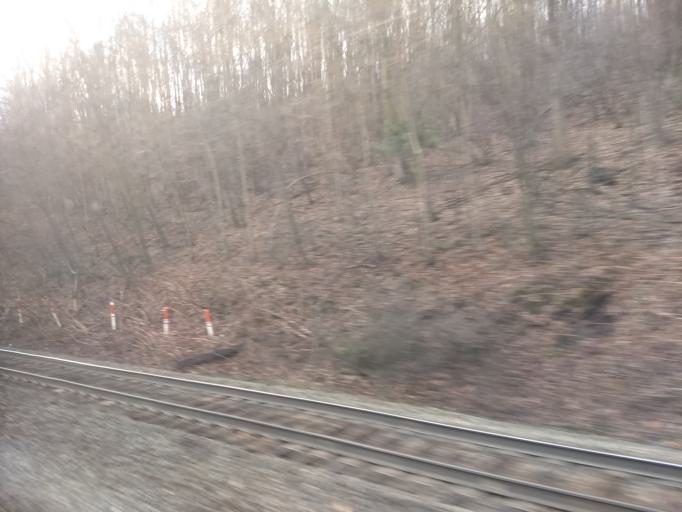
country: US
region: Pennsylvania
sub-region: Cambria County
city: Vinco
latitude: 40.3728
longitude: -78.8271
